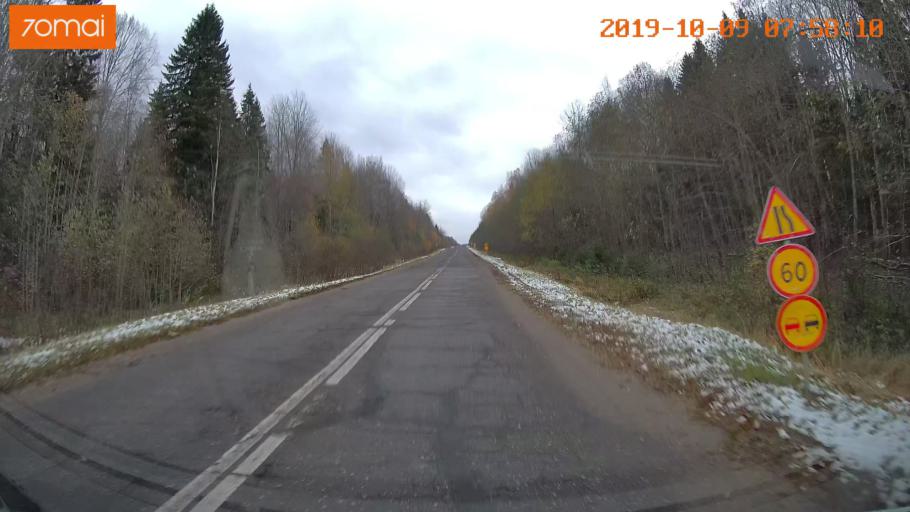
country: RU
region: Jaroslavl
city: Kukoboy
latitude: 58.6970
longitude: 39.9619
